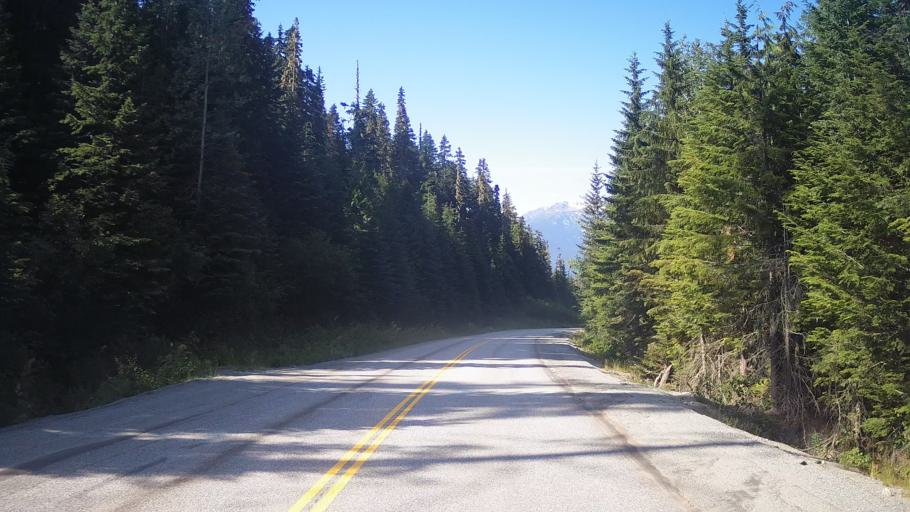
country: CA
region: British Columbia
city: Pemberton
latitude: 50.3604
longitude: -122.5232
